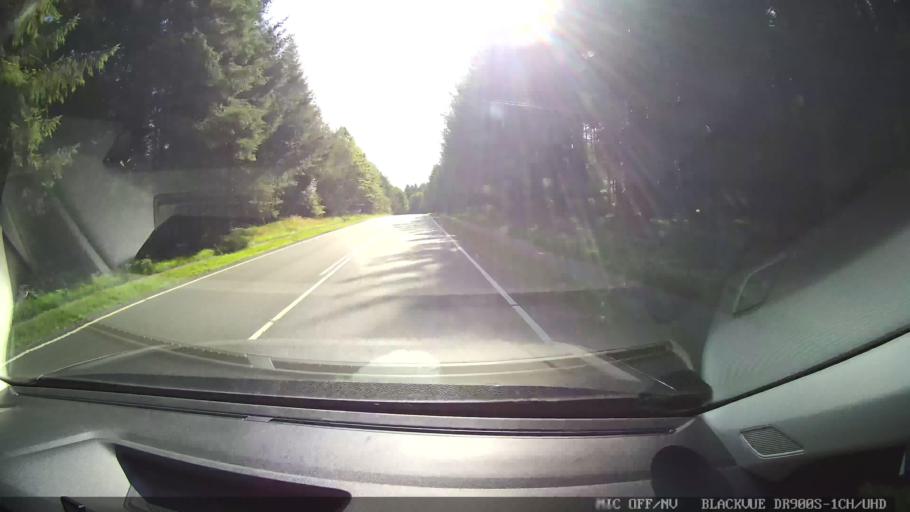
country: DK
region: North Denmark
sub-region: Mariagerfjord Kommune
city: Arden
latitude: 56.7799
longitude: 9.7587
